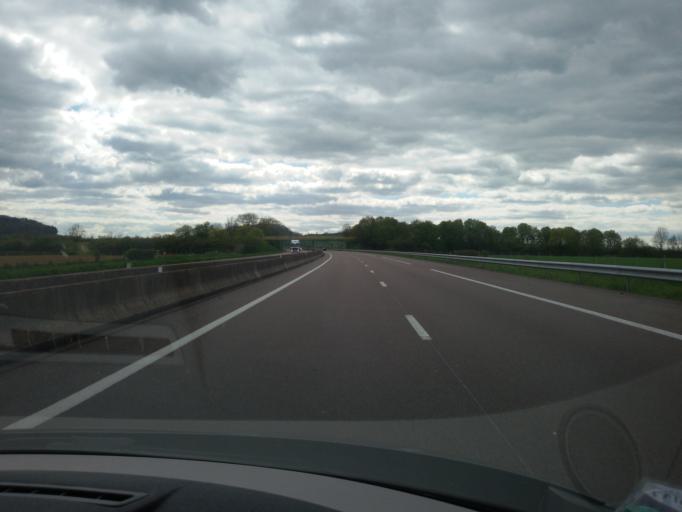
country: FR
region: Bourgogne
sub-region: Departement de la Cote-d'Or
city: Pouilly-en-Auxois
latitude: 47.2604
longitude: 4.5235
